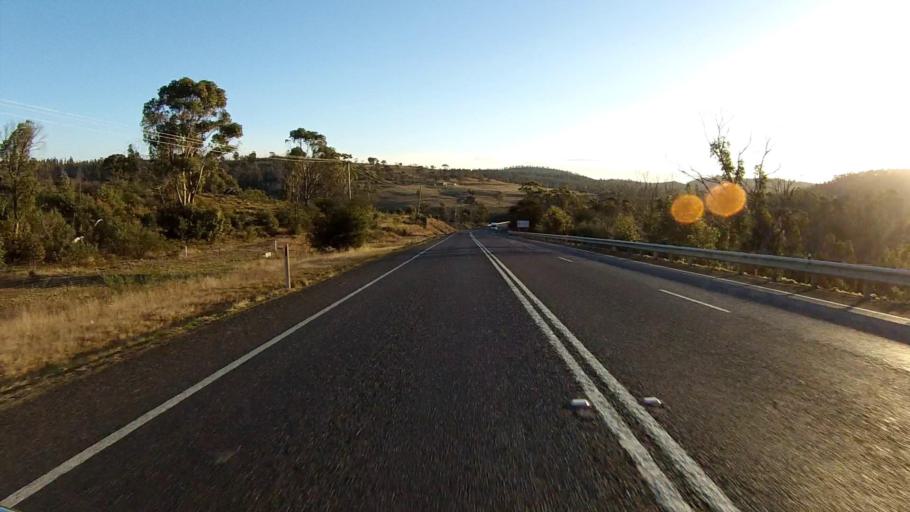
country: AU
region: Tasmania
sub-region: Sorell
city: Sorell
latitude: -42.8241
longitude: 147.7190
